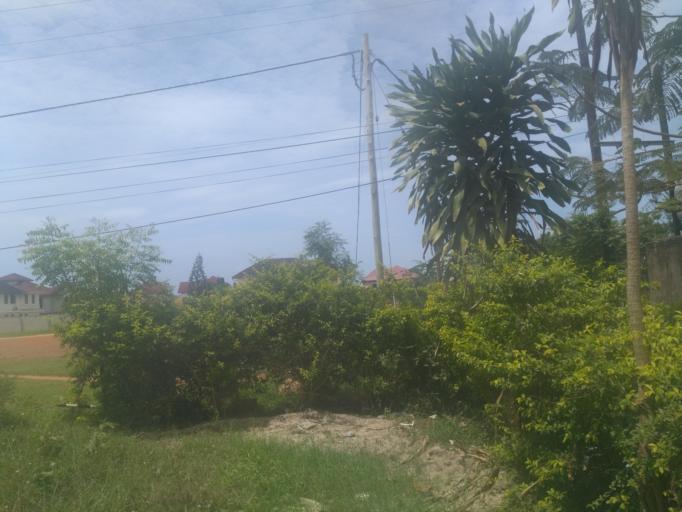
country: TZ
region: Zanzibar Urban/West
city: Zanzibar
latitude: -6.2211
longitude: 39.2134
